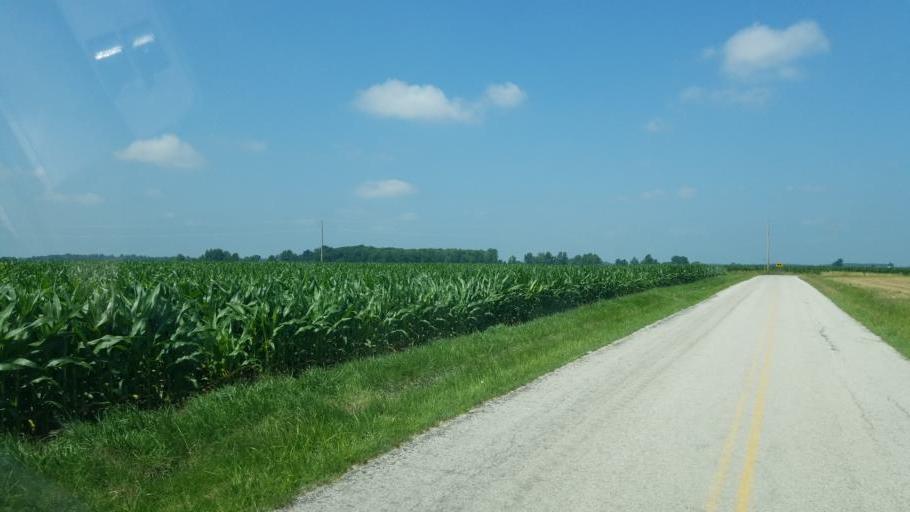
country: US
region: Ohio
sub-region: Huron County
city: Willard
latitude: 40.9846
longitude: -82.8806
